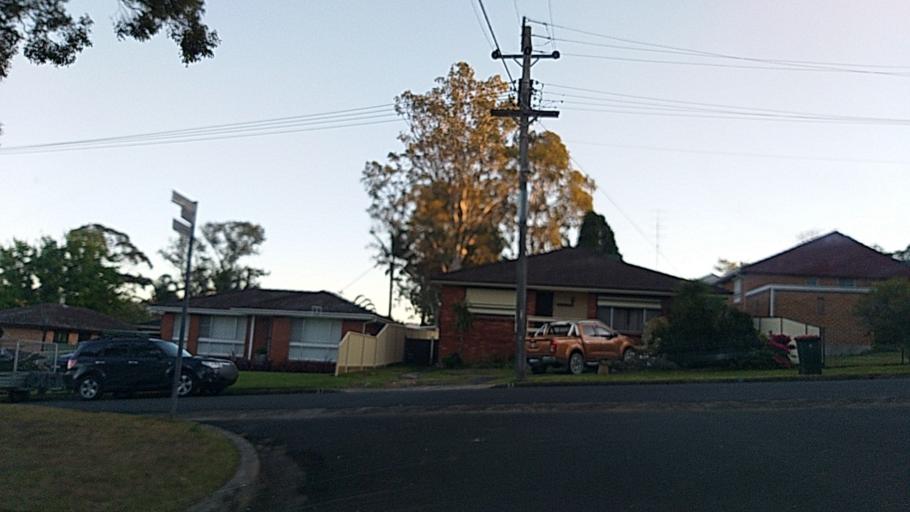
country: AU
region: New South Wales
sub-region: Wollongong
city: Dapto
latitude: -34.5119
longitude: 150.7827
